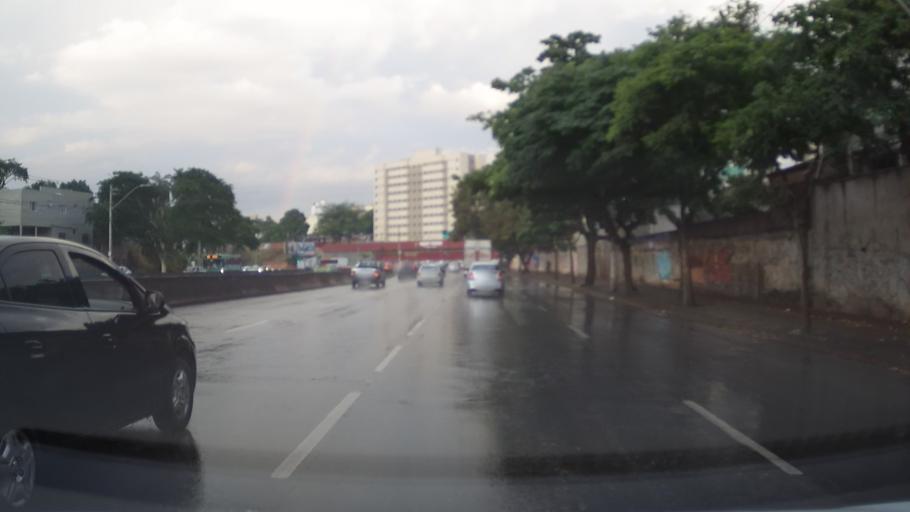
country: BR
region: Minas Gerais
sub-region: Belo Horizonte
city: Belo Horizonte
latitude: -19.9413
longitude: -43.9865
